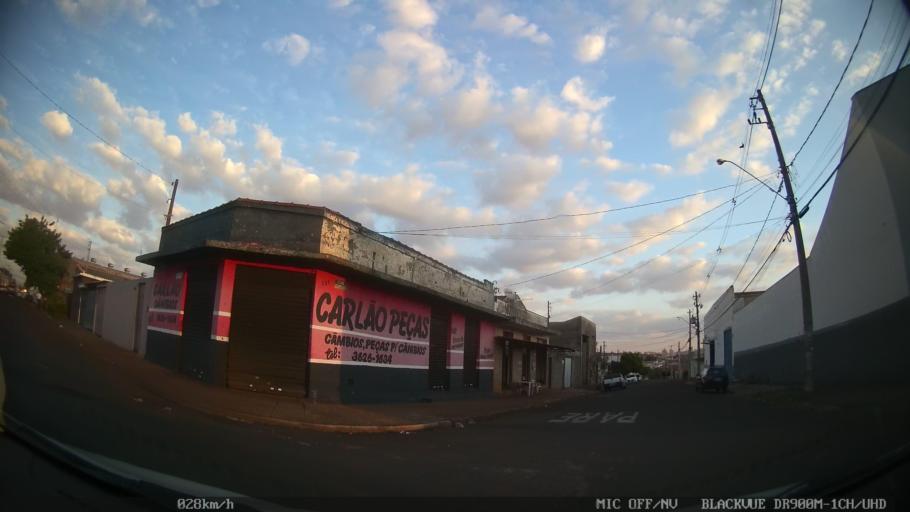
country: BR
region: Sao Paulo
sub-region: Ribeirao Preto
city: Ribeirao Preto
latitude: -21.1472
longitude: -47.7912
